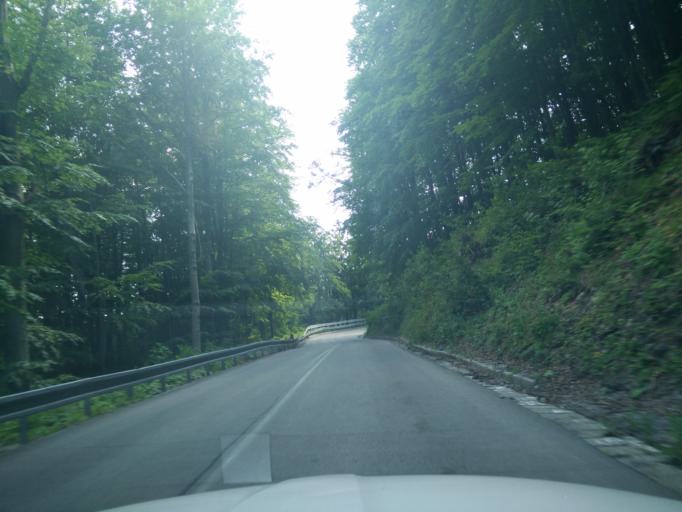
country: SK
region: Zilinsky
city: Rajec
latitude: 48.9543
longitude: 18.6213
